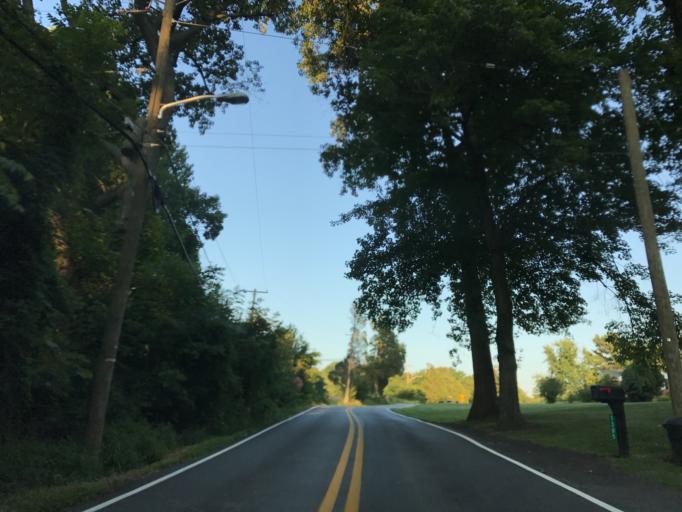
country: US
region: Maryland
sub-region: Baltimore County
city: Kingsville
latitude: 39.4320
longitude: -76.4231
